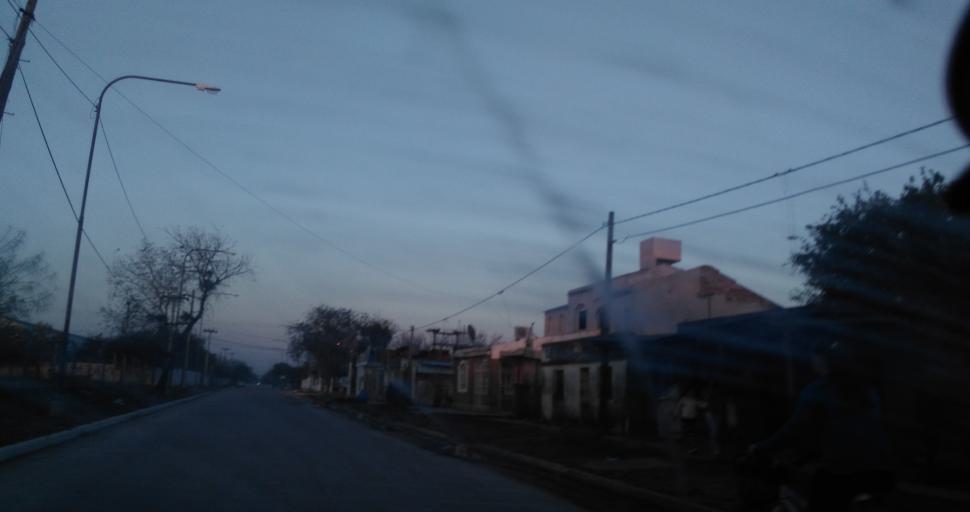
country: AR
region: Chaco
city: Resistencia
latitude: -27.4756
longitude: -58.9644
